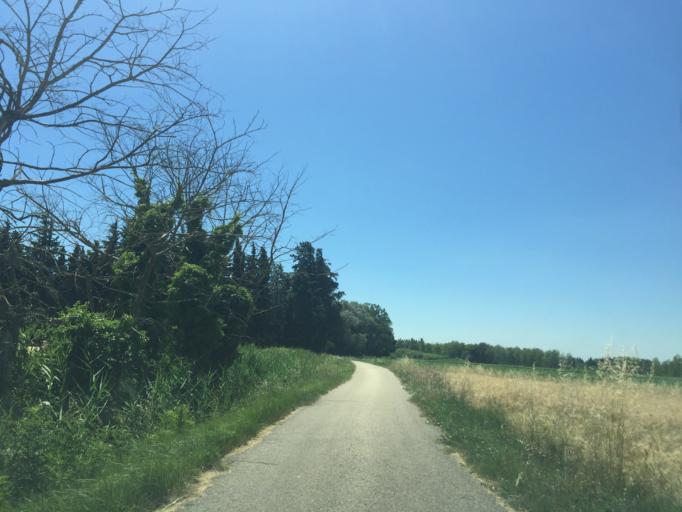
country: FR
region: Provence-Alpes-Cote d'Azur
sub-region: Departement du Vaucluse
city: Caderousse
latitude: 44.1141
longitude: 4.7673
